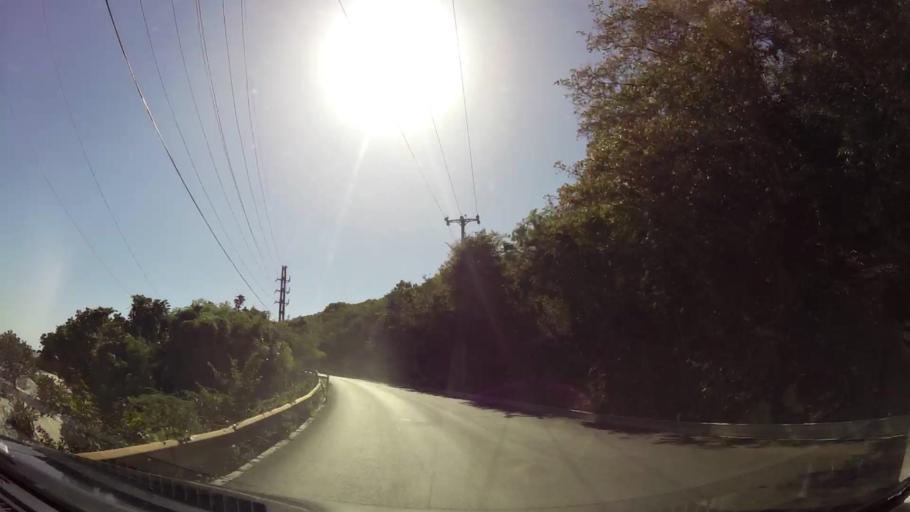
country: VG
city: Tortola
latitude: 18.4156
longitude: -64.5877
